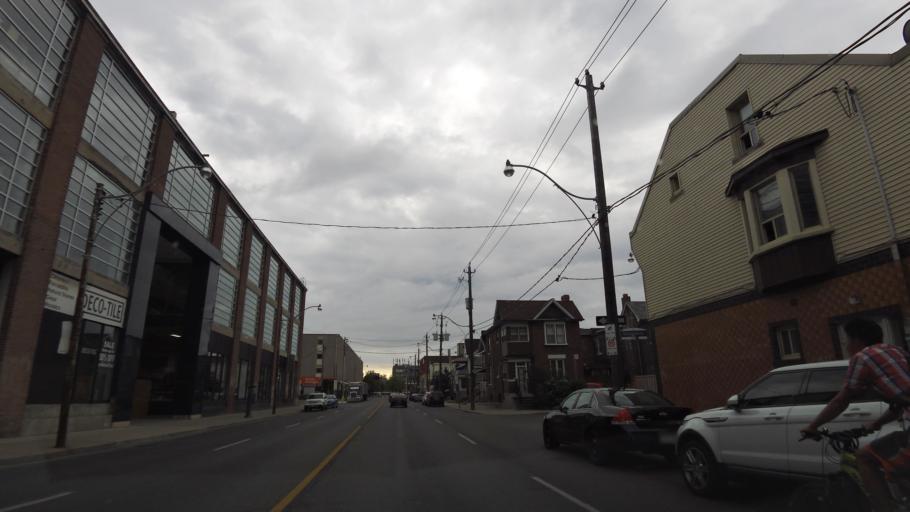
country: CA
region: Ontario
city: Toronto
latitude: 43.6699
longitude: -79.4319
